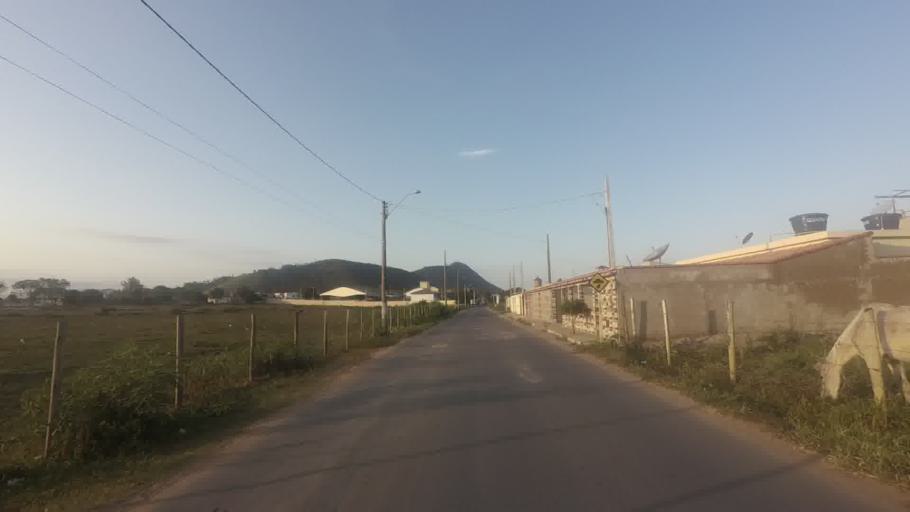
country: BR
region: Espirito Santo
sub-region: Piuma
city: Piuma
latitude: -20.8931
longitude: -40.7836
